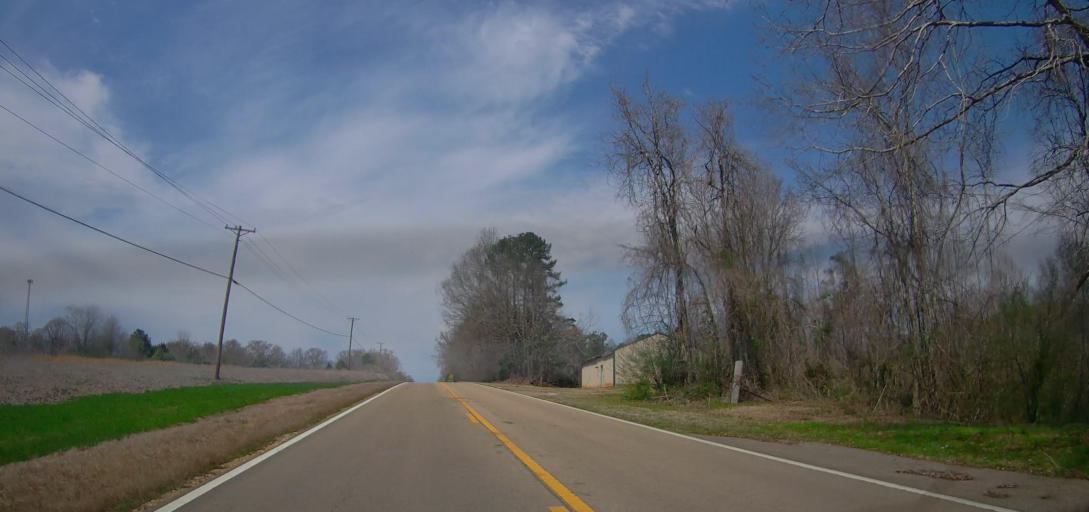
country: US
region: Mississippi
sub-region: Union County
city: New Albany
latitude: 34.4337
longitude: -88.9542
